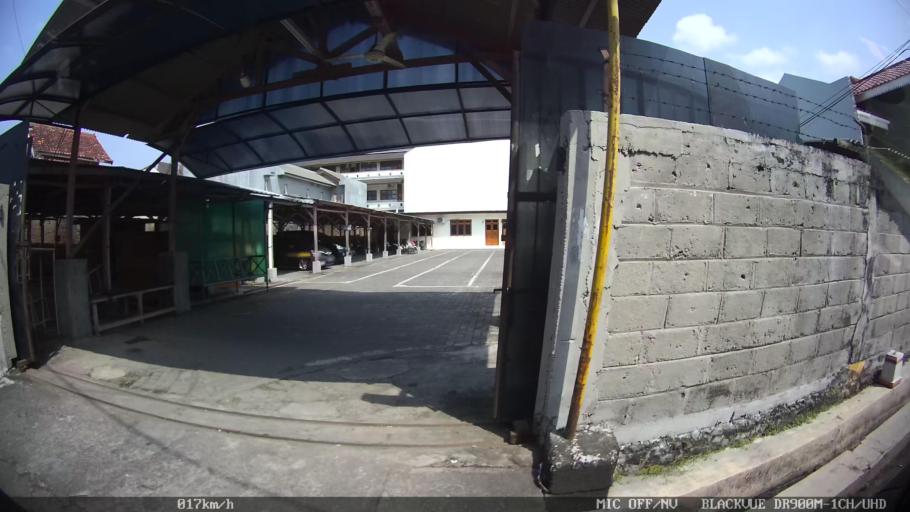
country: ID
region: Daerah Istimewa Yogyakarta
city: Yogyakarta
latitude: -7.8092
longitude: 110.3899
